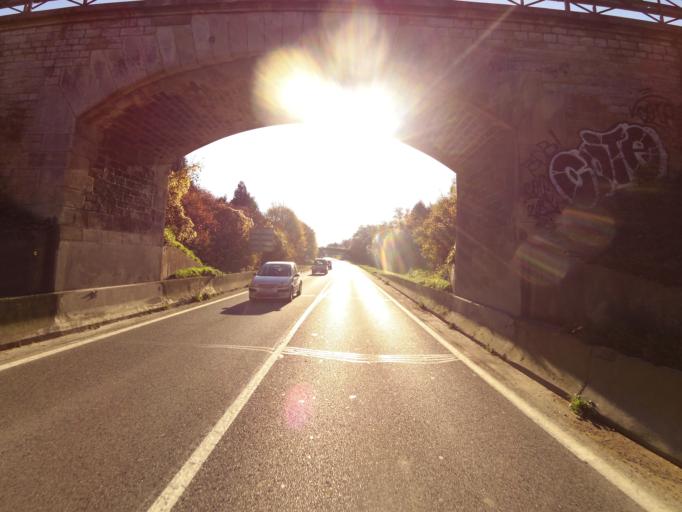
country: FR
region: Champagne-Ardenne
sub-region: Departement de l'Aube
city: Breviandes
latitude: 48.2595
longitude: 4.0970
